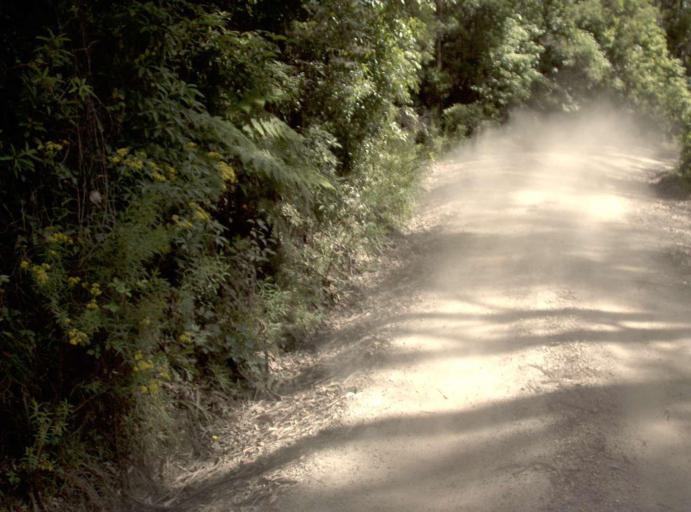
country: AU
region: Victoria
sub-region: East Gippsland
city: Lakes Entrance
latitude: -37.6020
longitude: 148.7133
